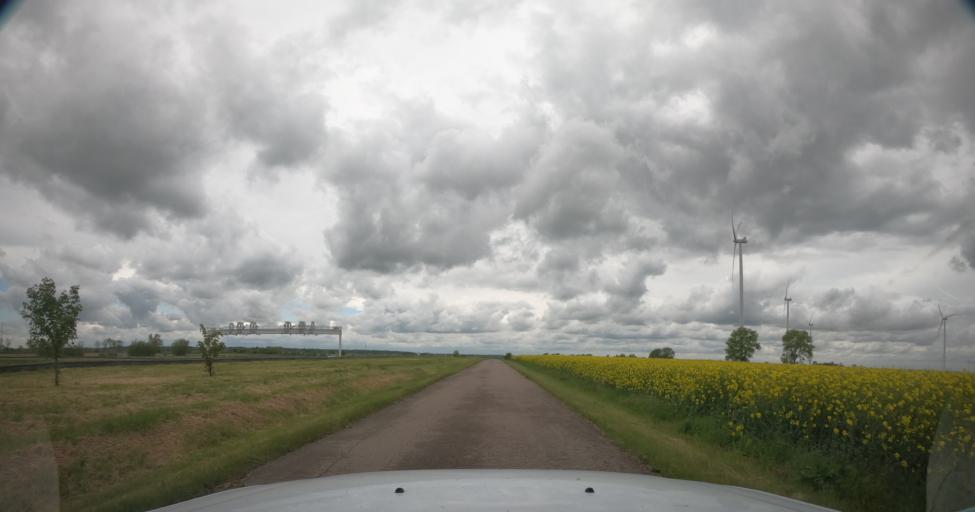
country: PL
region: West Pomeranian Voivodeship
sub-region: Powiat pyrzycki
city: Kozielice
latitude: 53.0992
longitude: 14.8039
